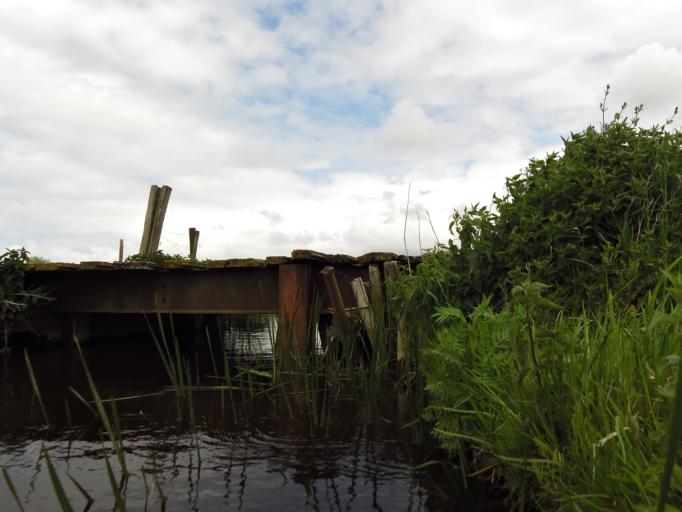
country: NL
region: South Holland
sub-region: Gemeente Wassenaar
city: Wassenaar
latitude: 52.1116
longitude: 4.3904
